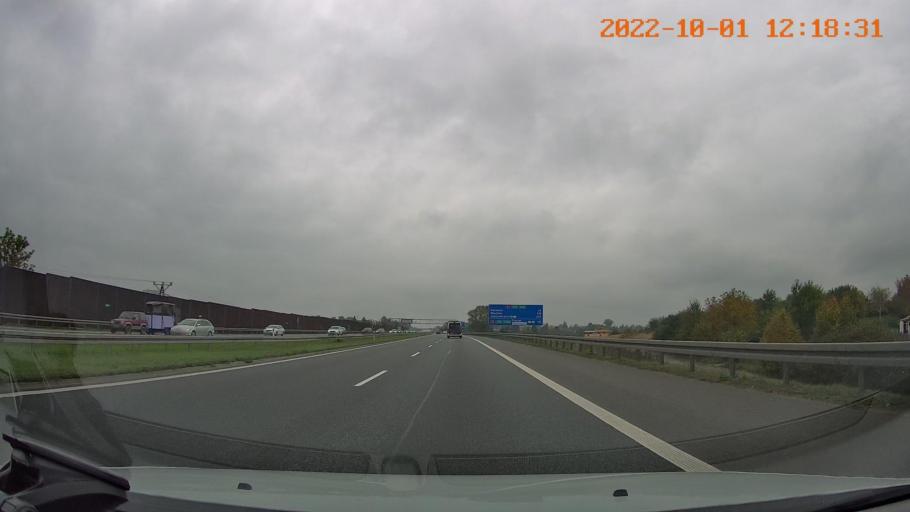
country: PL
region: Lesser Poland Voivodeship
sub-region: Powiat chrzanowski
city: Chrzanow
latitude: 50.1507
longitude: 19.4151
